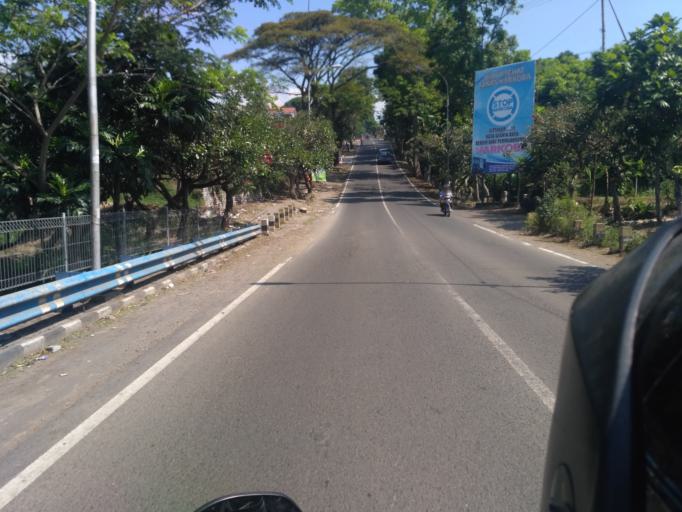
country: ID
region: East Java
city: Batu
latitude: -7.8645
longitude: 112.5476
